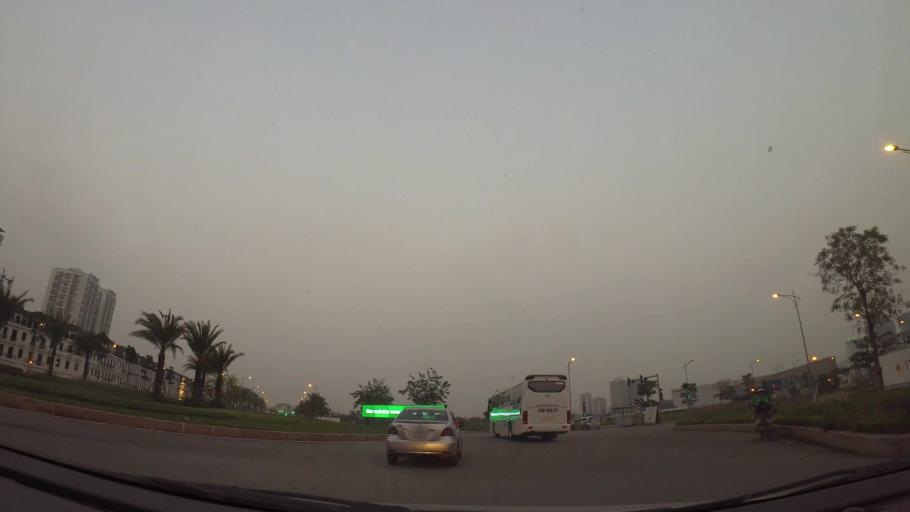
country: VN
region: Ha Noi
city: Tay Ho
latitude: 21.0624
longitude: 105.7974
